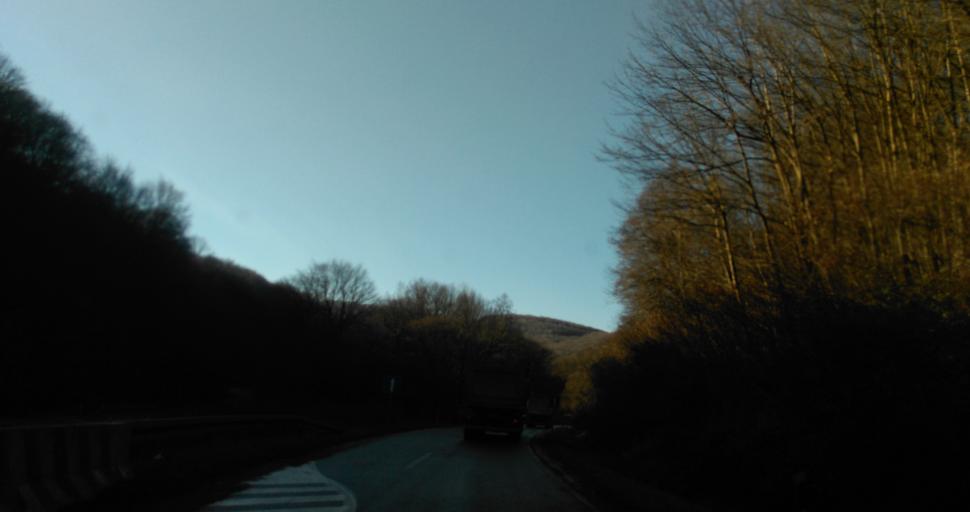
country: RS
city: Vrdnik
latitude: 45.1760
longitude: 19.8348
